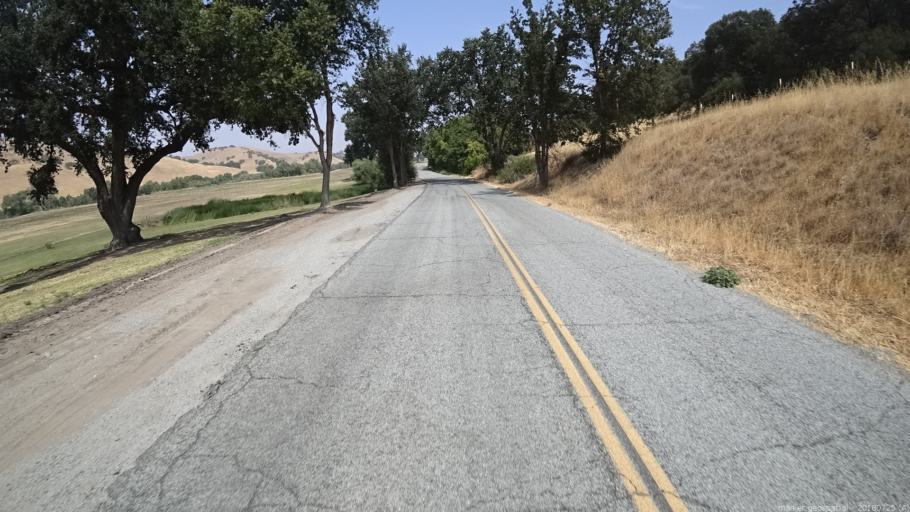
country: US
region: California
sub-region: San Luis Obispo County
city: San Miguel
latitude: 35.8033
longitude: -120.6765
